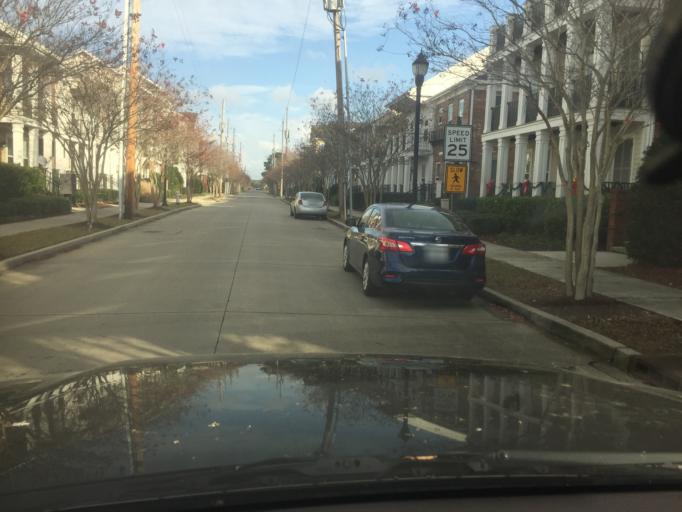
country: US
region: Louisiana
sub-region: Orleans Parish
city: New Orleans
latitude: 29.9948
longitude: -90.0768
